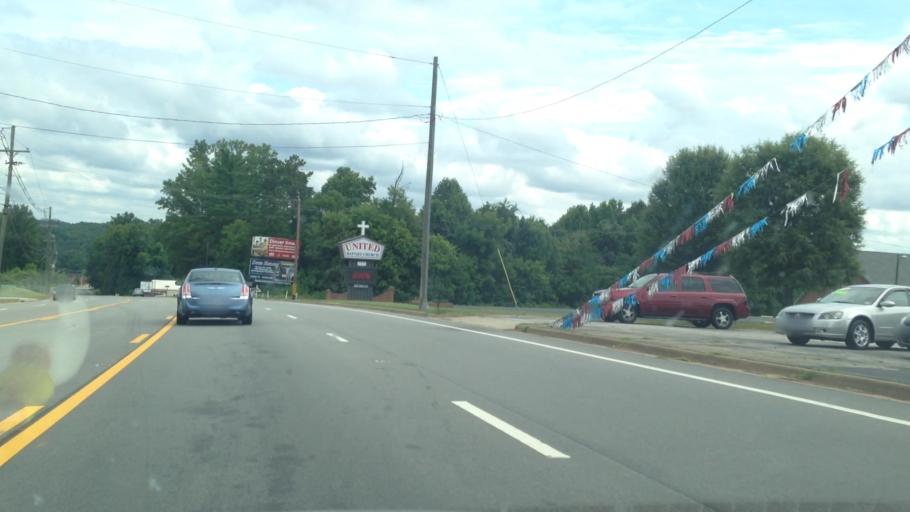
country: US
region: Virginia
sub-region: Pittsylvania County
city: Mount Hermon
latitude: 36.6421
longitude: -79.3824
